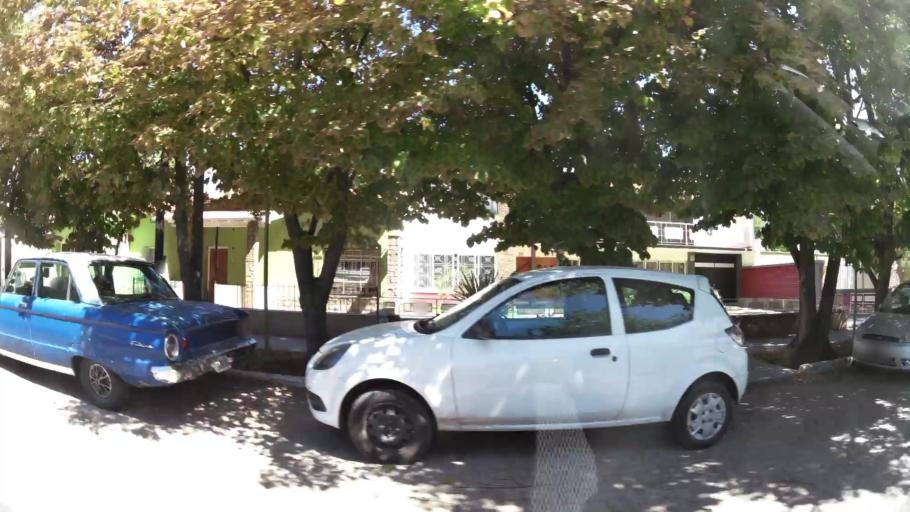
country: AR
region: Mendoza
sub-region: Departamento de Godoy Cruz
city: Godoy Cruz
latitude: -32.9598
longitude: -68.8528
